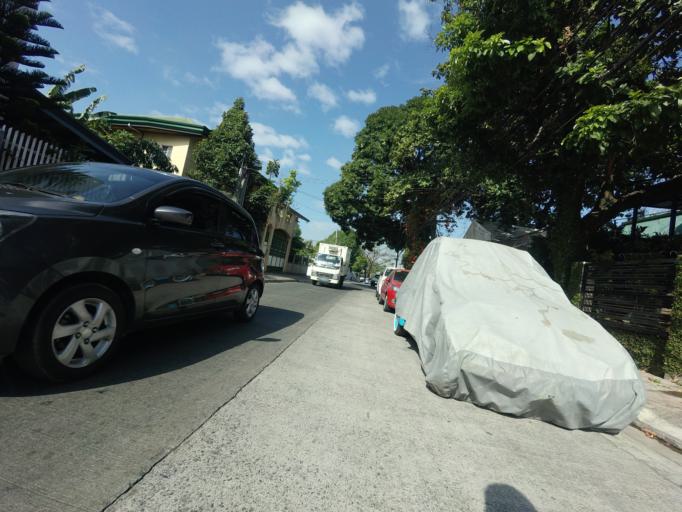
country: PH
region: Calabarzon
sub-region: Province of Rizal
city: Antipolo
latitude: 14.6432
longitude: 121.1153
